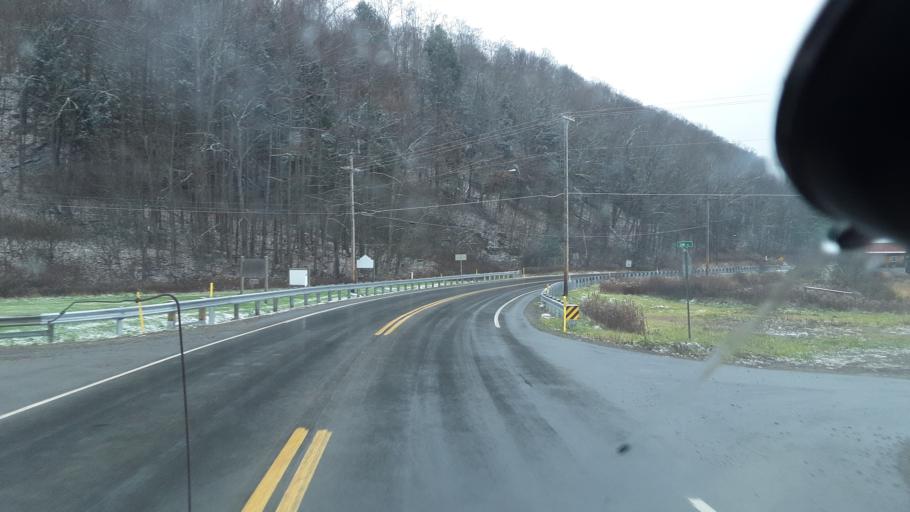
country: US
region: Pennsylvania
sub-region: Potter County
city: Shinglehouse
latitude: 41.9619
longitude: -78.2010
